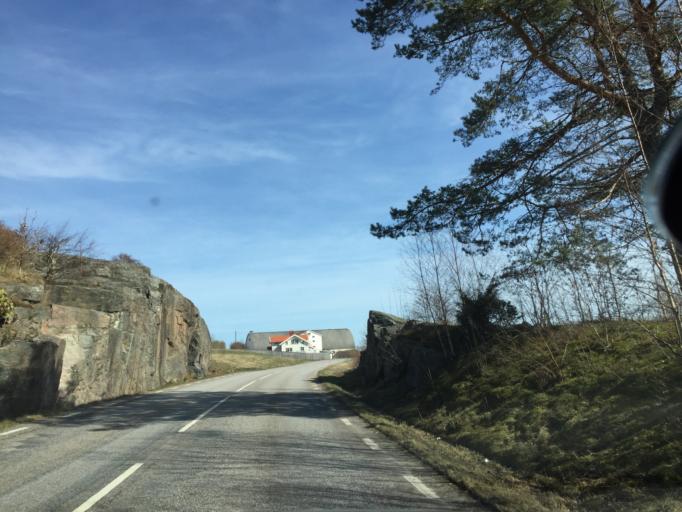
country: SE
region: Vaestra Goetaland
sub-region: Orust
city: Henan
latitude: 58.3422
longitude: 11.7346
